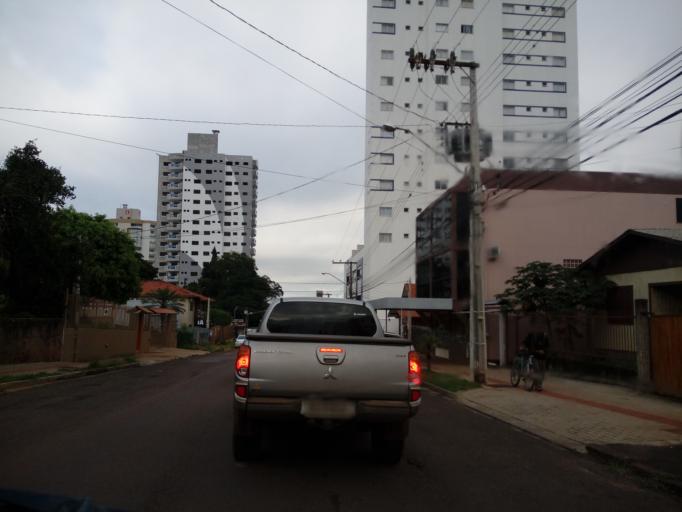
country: BR
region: Santa Catarina
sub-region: Chapeco
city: Chapeco
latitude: -27.0908
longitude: -52.6136
